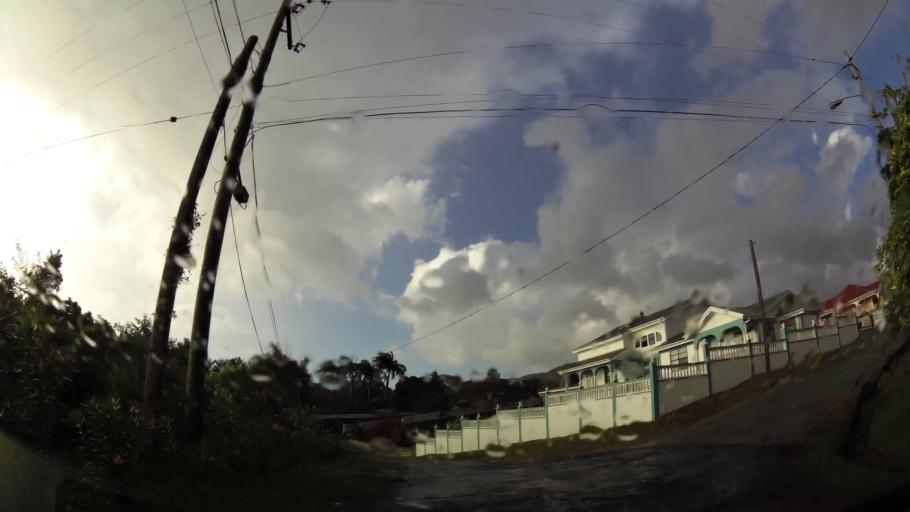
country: DM
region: Saint Paul
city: Mahaut
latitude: 15.3652
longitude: -61.3987
